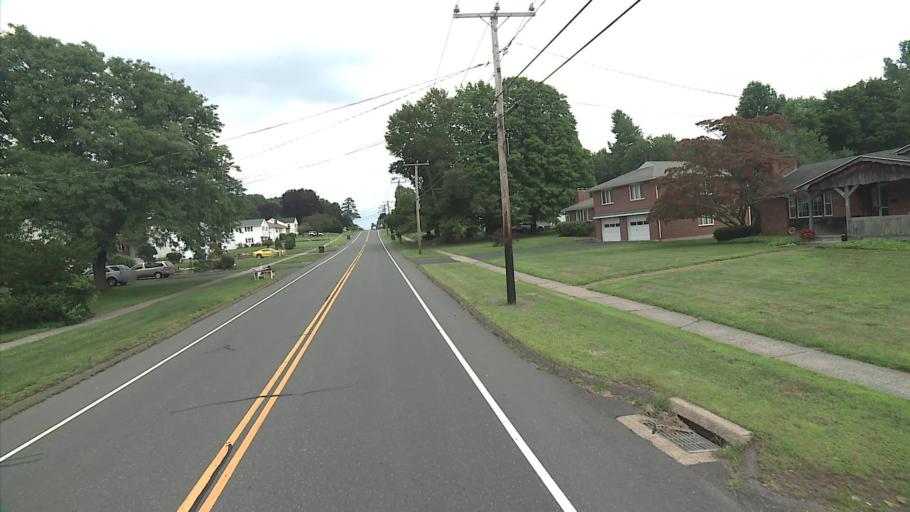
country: US
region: Connecticut
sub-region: Hartford County
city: Wethersfield
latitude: 41.6949
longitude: -72.6647
